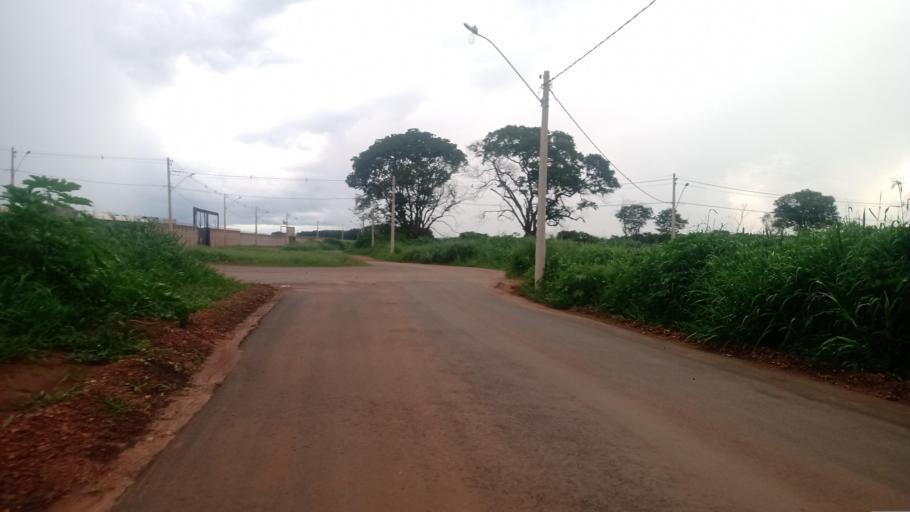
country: BR
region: Goias
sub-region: Senador Canedo
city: Senador Canedo
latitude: -16.7167
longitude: -49.1202
